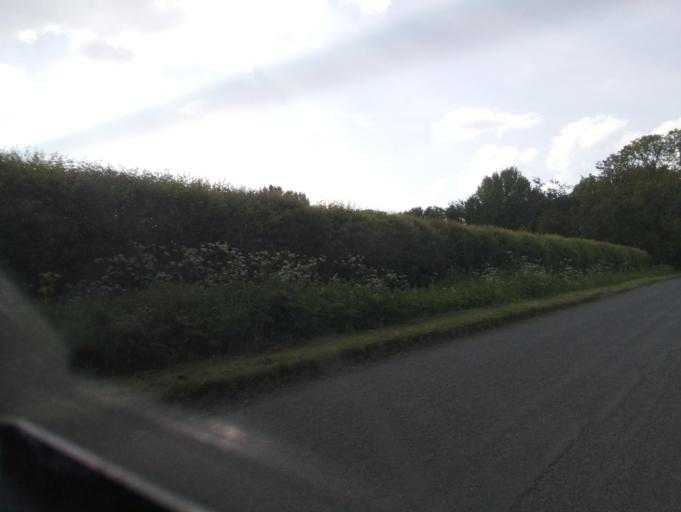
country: GB
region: England
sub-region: Wiltshire
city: Luckington
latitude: 51.5924
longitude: -2.2331
